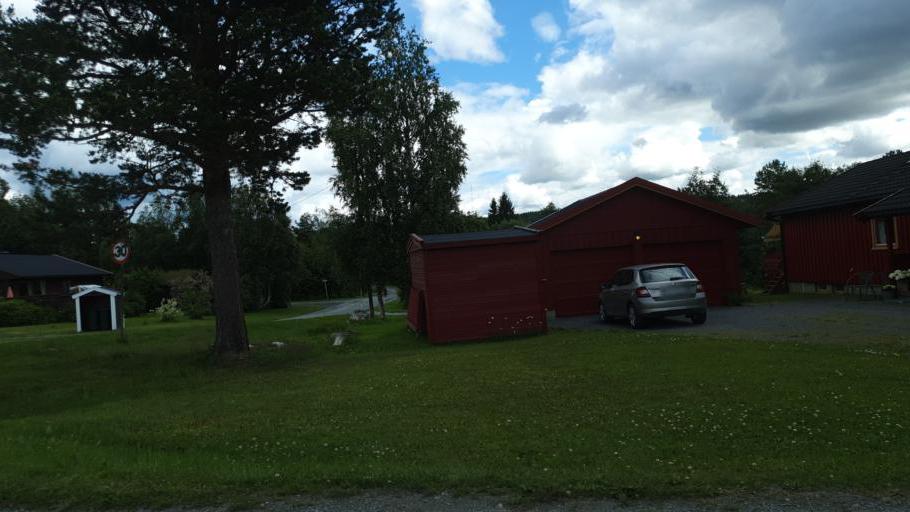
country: NO
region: Sor-Trondelag
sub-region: Rennebu
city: Berkak
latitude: 62.8313
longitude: 10.0036
